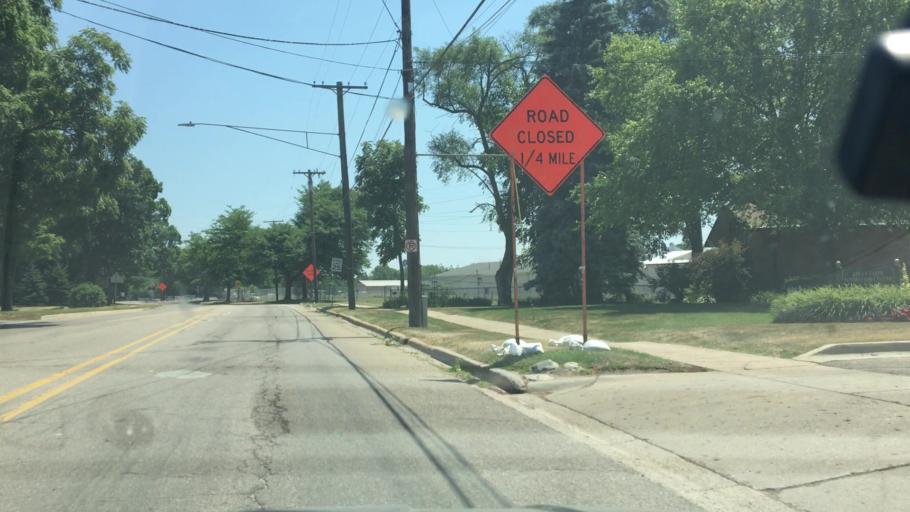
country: US
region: Michigan
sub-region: Livingston County
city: Brighton
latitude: 42.5232
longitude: -83.7769
